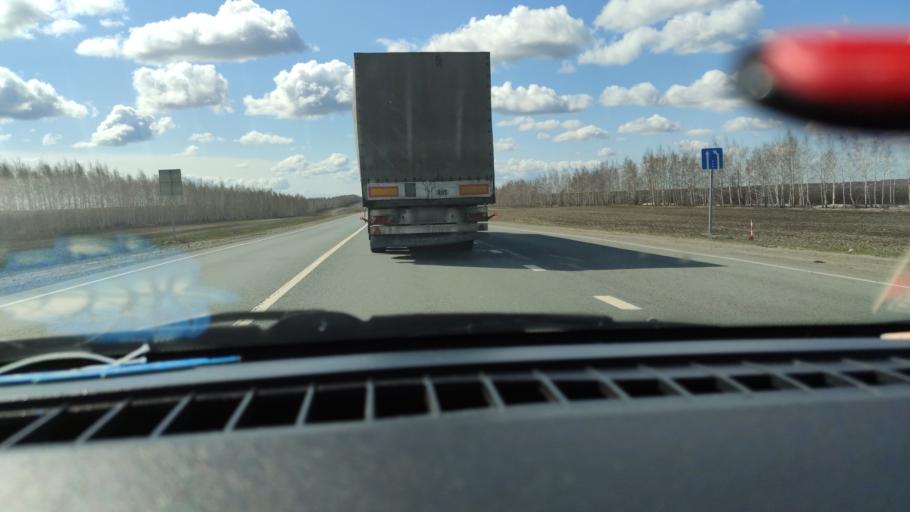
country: RU
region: Samara
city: Syzran'
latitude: 52.9155
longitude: 48.3010
